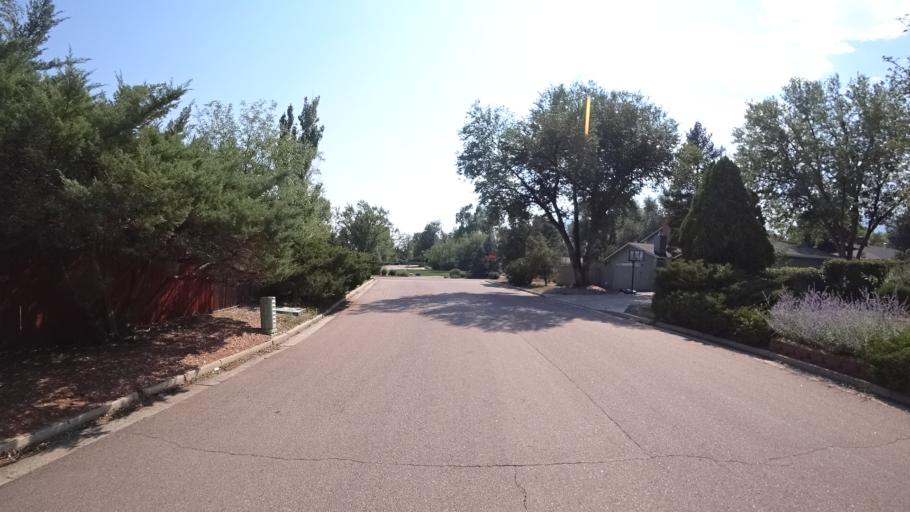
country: US
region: Colorado
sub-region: El Paso County
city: Colorado Springs
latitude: 38.8016
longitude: -104.8298
